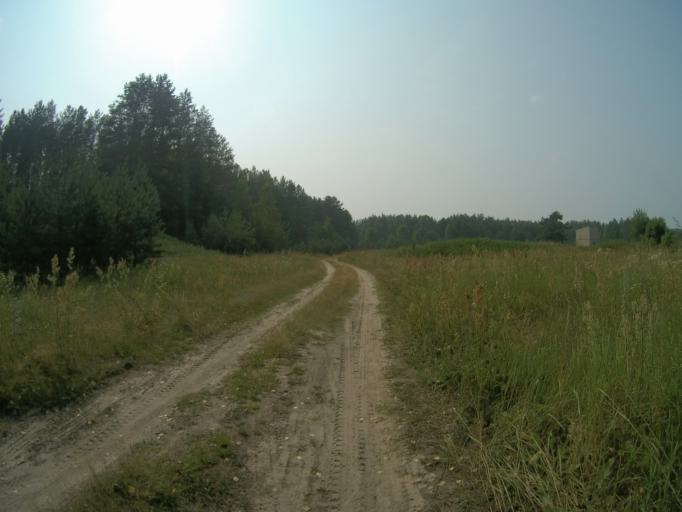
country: RU
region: Vladimir
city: Vorsha
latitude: 55.9671
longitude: 40.1806
